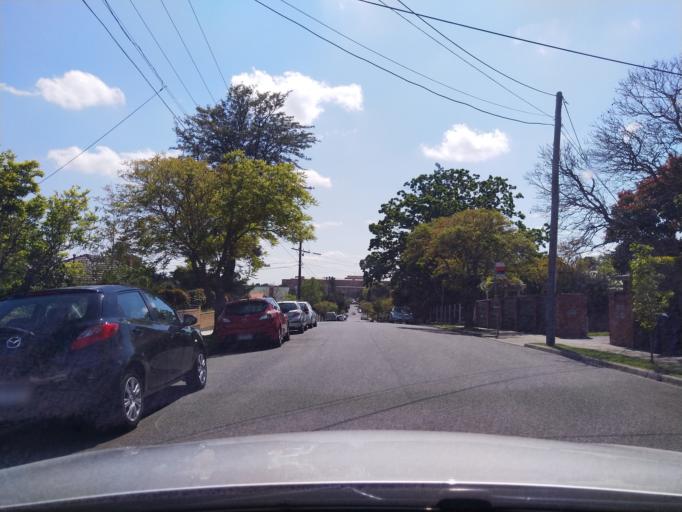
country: AU
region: Victoria
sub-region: Banyule
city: Bellfield
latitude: -37.7610
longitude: 145.0465
